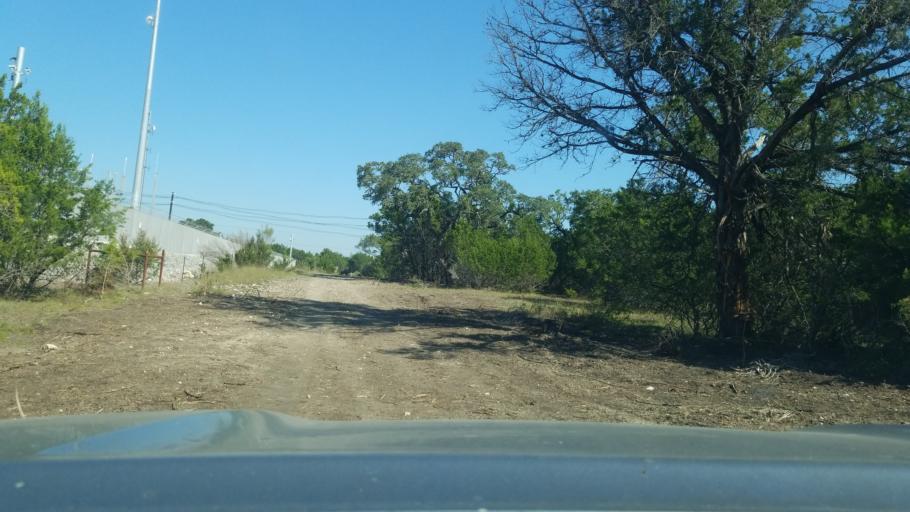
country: US
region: Texas
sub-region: Kendall County
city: Boerne
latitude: 29.7617
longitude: -98.7196
